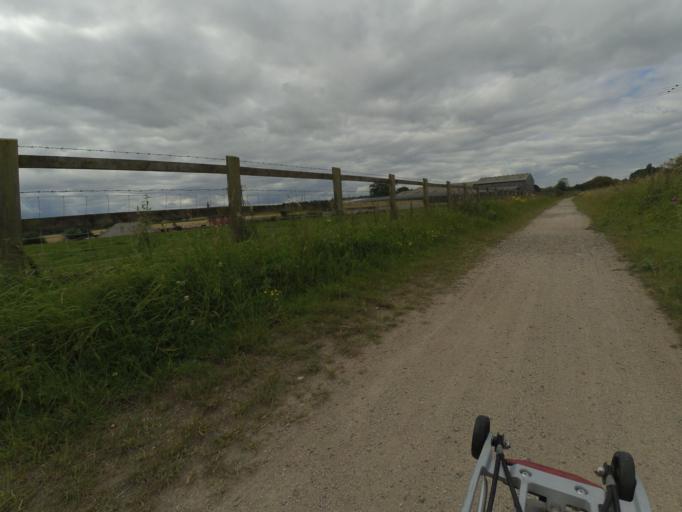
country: GB
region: England
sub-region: Staffordshire
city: Gnosall
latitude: 52.7807
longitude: -2.2438
